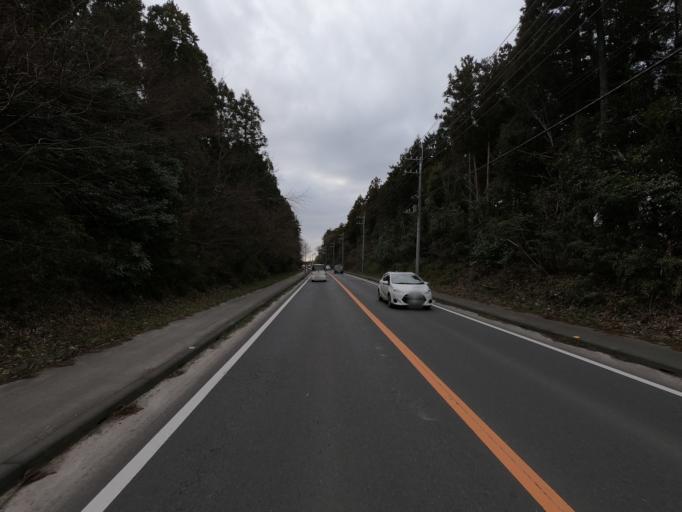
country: JP
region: Ibaraki
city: Ishioka
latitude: 36.0899
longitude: 140.3111
